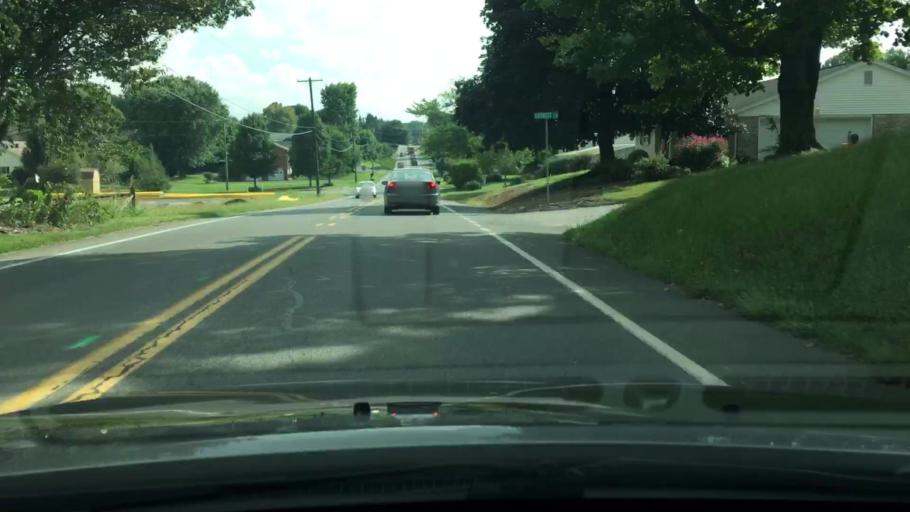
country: US
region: Pennsylvania
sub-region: Franklin County
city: Guilford
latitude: 39.9248
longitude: -77.5915
